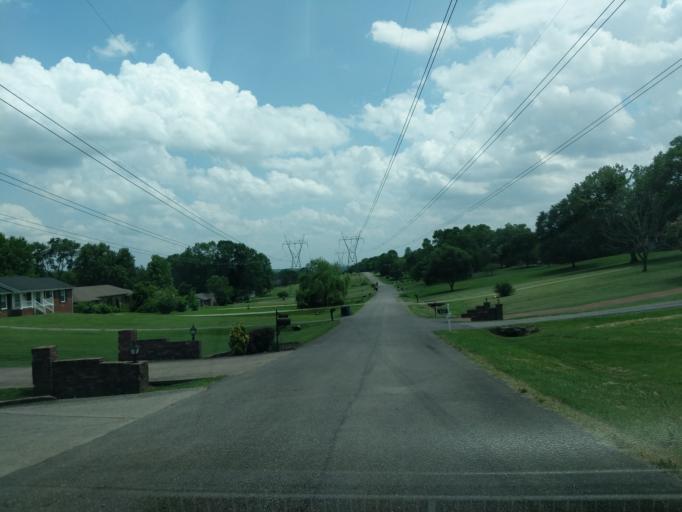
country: US
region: Tennessee
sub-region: Davidson County
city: Goodlettsville
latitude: 36.3095
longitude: -86.7280
